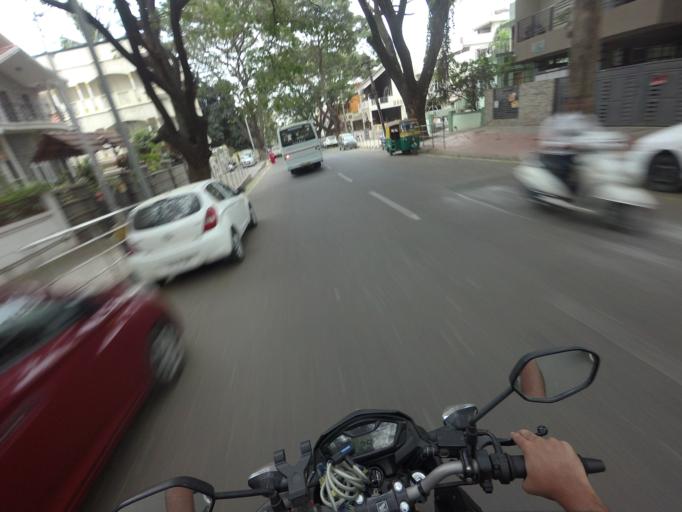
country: IN
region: Karnataka
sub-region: Bangalore Urban
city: Bangalore
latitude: 12.9636
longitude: 77.5409
